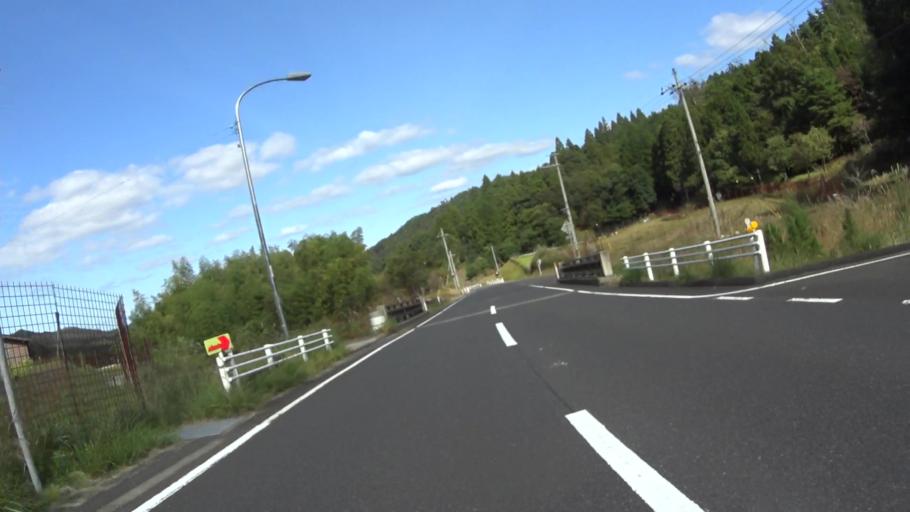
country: JP
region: Hyogo
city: Toyooka
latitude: 35.5408
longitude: 134.9771
